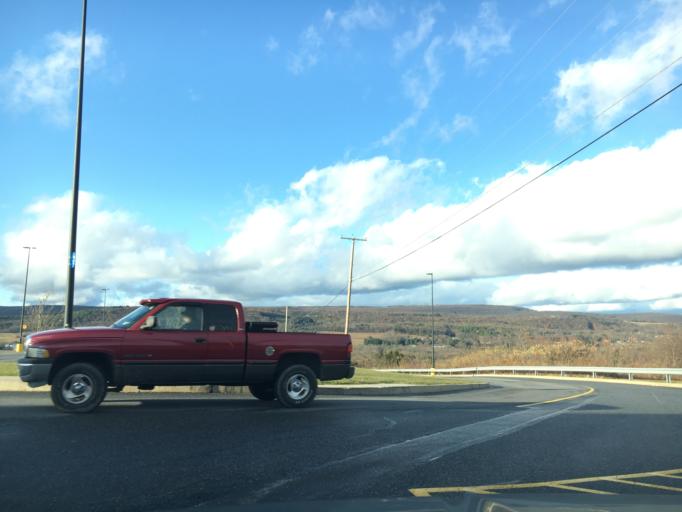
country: US
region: Pennsylvania
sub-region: Carbon County
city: Lehighton
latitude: 40.8107
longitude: -75.7375
